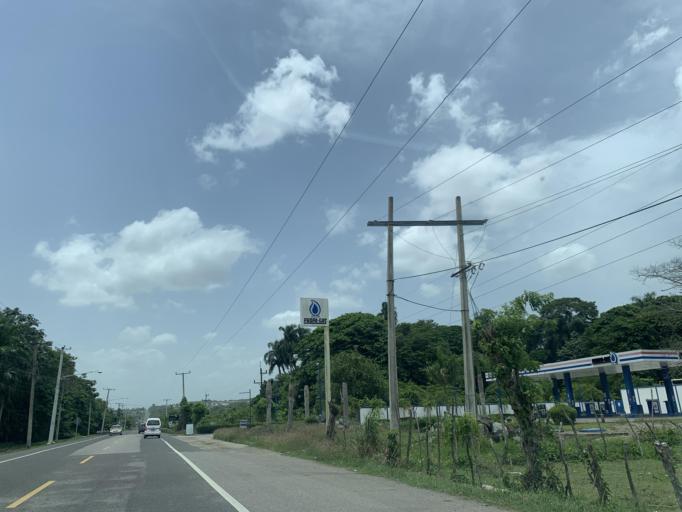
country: DO
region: Puerto Plata
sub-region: Puerto Plata
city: Puerto Plata
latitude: 19.7486
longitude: -70.6387
